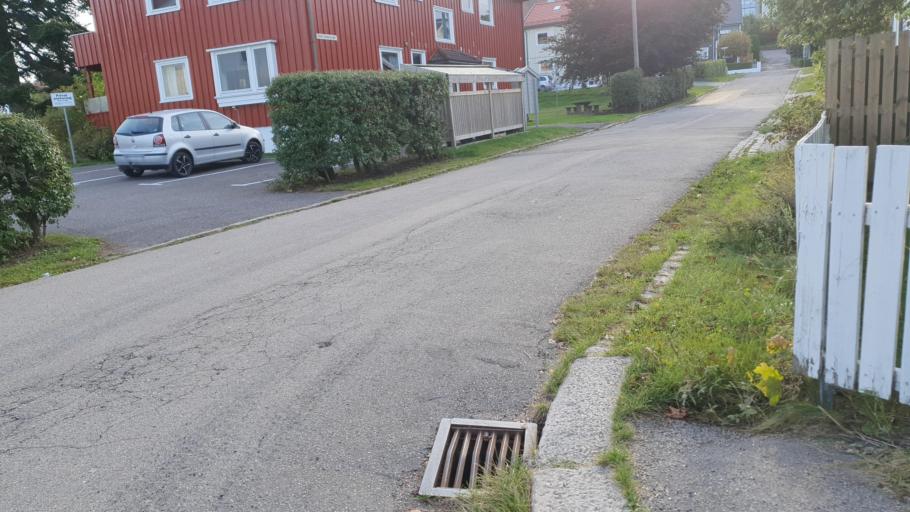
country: NO
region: Vestfold
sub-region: Tonsberg
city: Tonsberg
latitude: 59.2731
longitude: 10.4243
